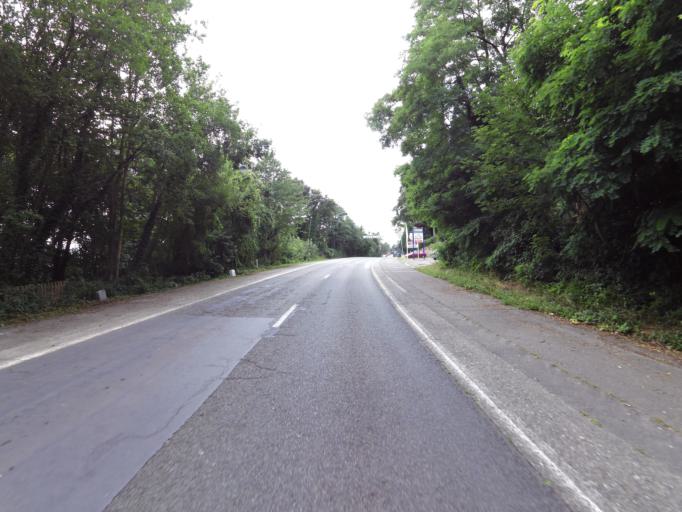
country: FR
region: Nord-Pas-de-Calais
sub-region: Departement du Nord
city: Saint-Jans-Cappel
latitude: 50.7834
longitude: 2.7481
